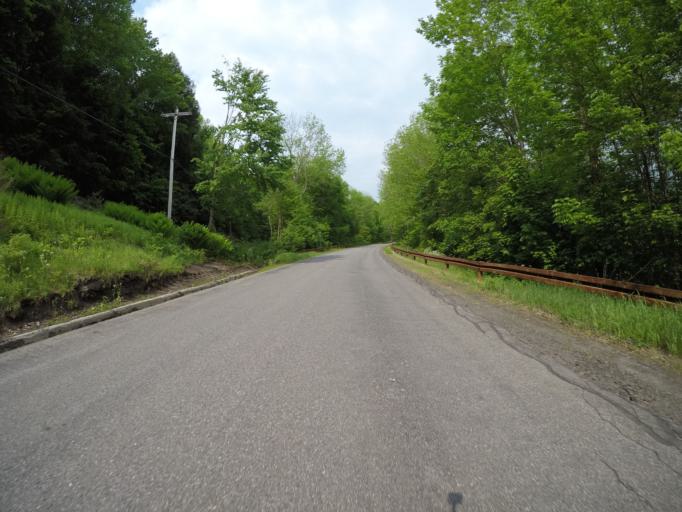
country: US
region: New York
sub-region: Sullivan County
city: Livingston Manor
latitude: 42.0821
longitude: -74.7896
